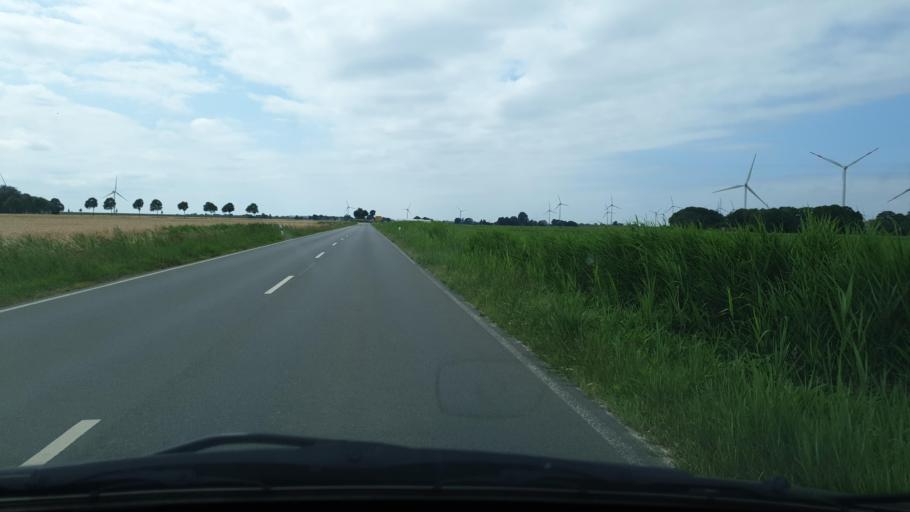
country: DE
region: Schleswig-Holstein
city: Marnerdeich
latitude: 53.9487
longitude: 8.9666
